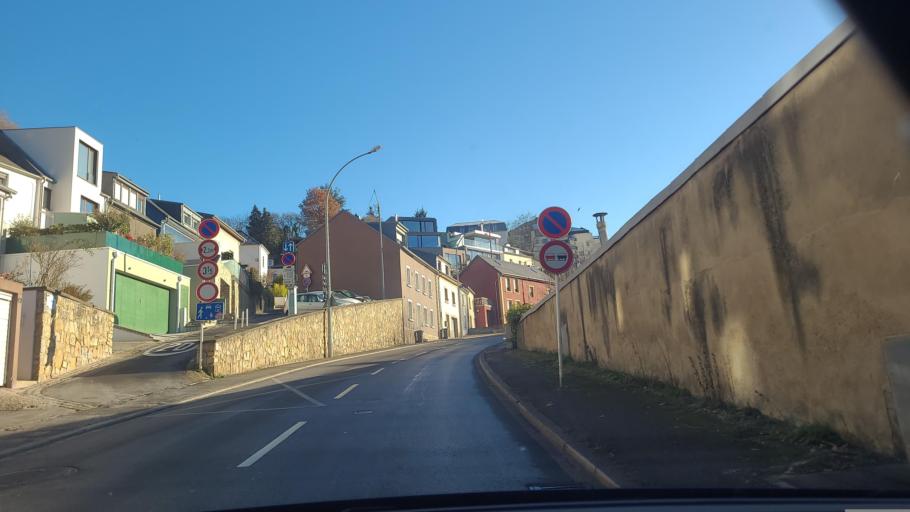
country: LU
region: Luxembourg
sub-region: Canton de Luxembourg
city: Luxembourg
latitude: 49.6243
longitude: 6.1058
